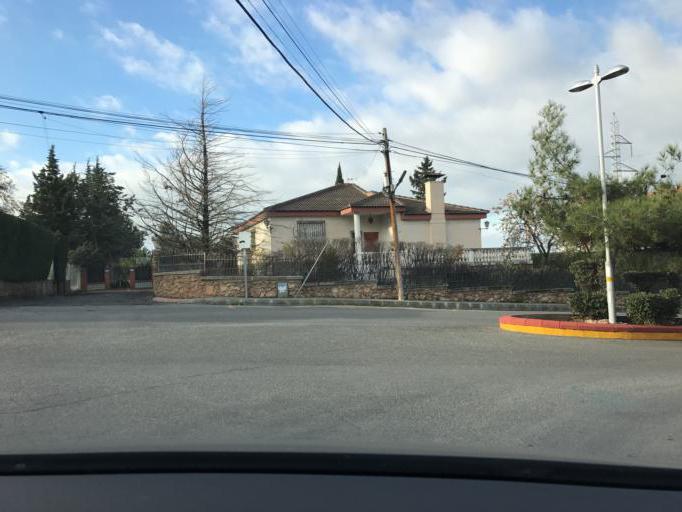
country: ES
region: Andalusia
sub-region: Provincia de Granada
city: Monachil
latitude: 37.1312
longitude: -3.5543
